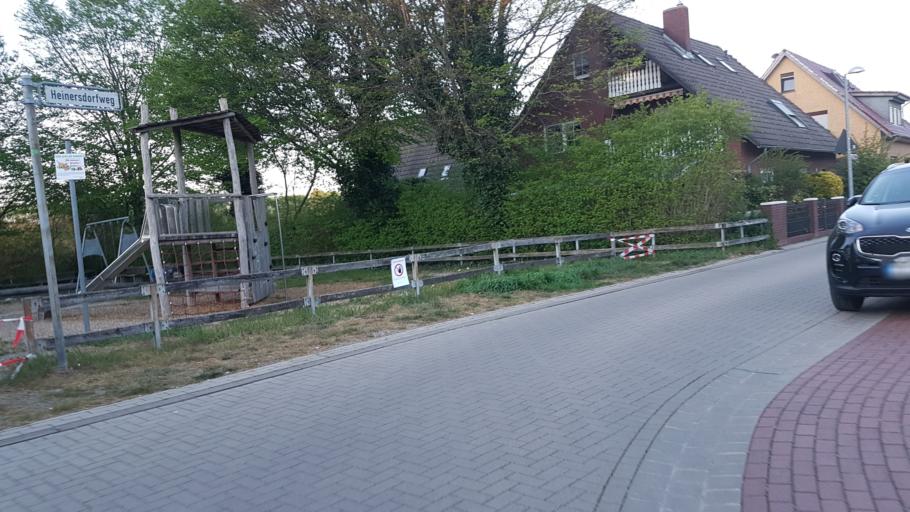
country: DE
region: Lower Saxony
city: Langenhagen
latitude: 52.4240
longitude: 9.7689
